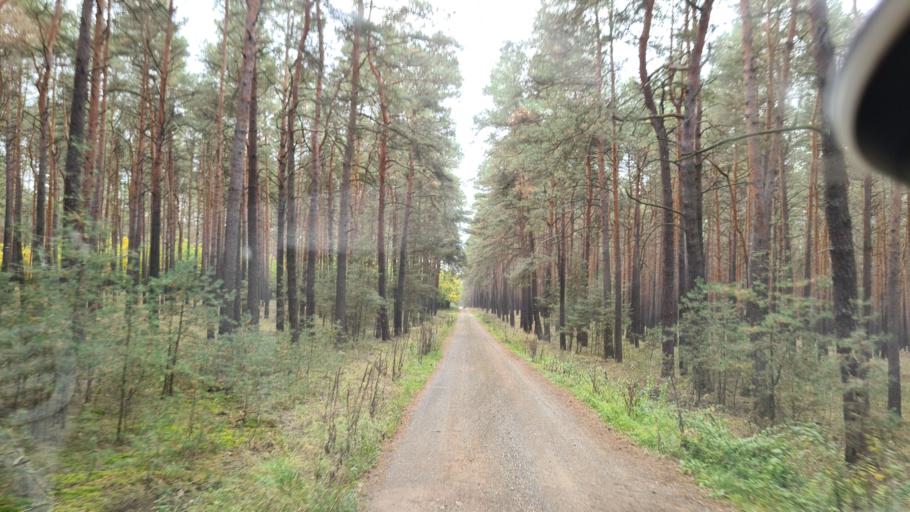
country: DE
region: Brandenburg
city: Schonewalde
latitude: 51.7084
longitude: 13.5777
